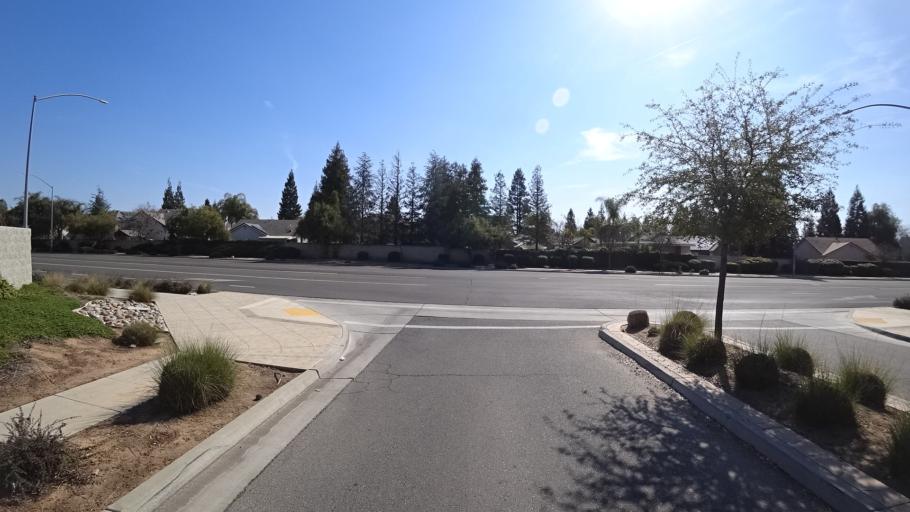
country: US
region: California
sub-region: Fresno County
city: Clovis
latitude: 36.8887
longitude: -119.7417
